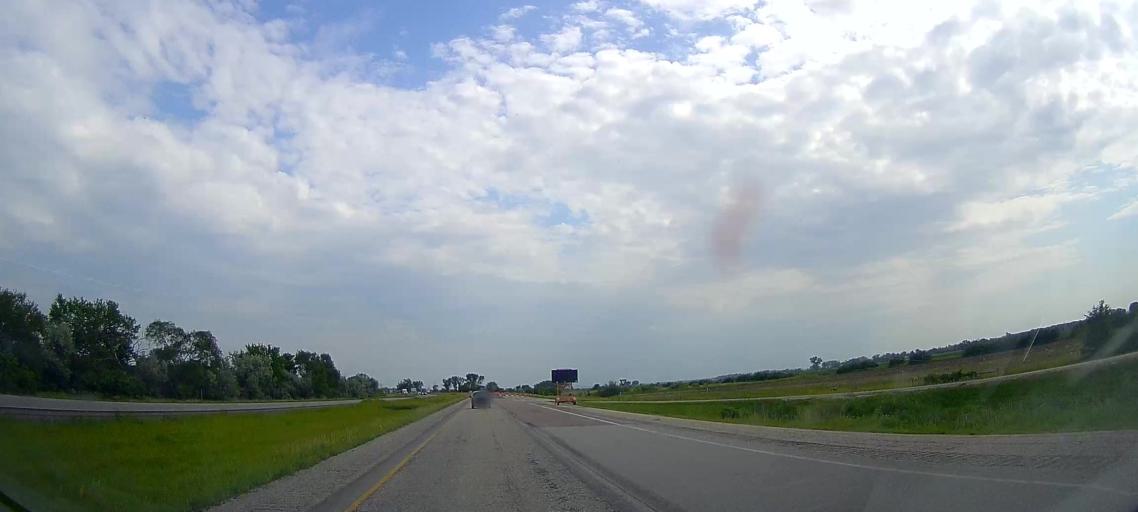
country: US
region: Nebraska
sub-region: Burt County
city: Tekamah
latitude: 41.7391
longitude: -96.0481
